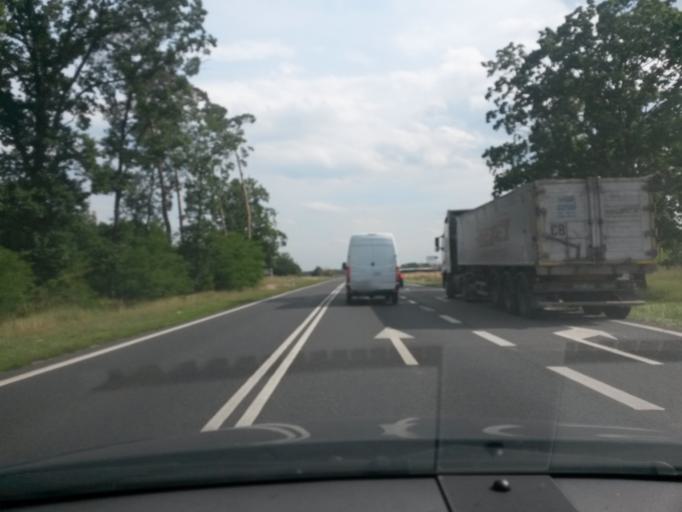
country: PL
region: Greater Poland Voivodeship
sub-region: Powiat sremski
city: Srem
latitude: 52.1330
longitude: 17.0418
